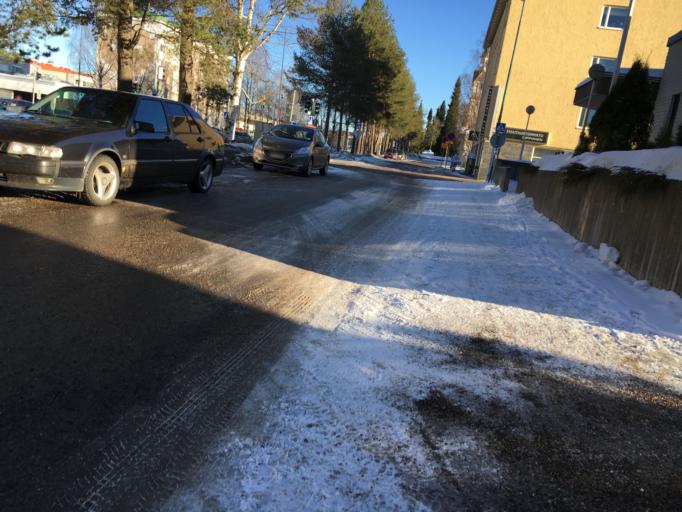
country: FI
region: Kainuu
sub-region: Kajaani
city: Kajaani
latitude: 64.2265
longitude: 27.7268
